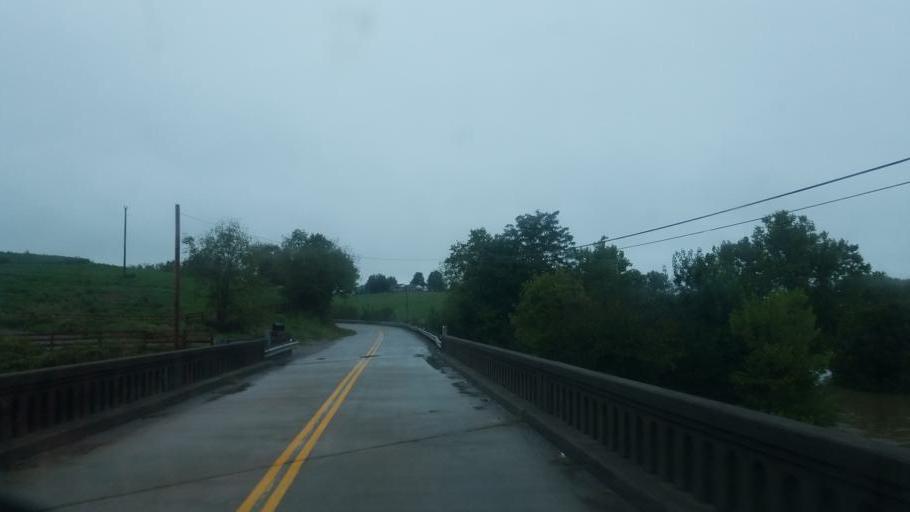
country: US
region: Kentucky
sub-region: Fleming County
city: Flemingsburg
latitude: 38.4164
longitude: -83.6964
